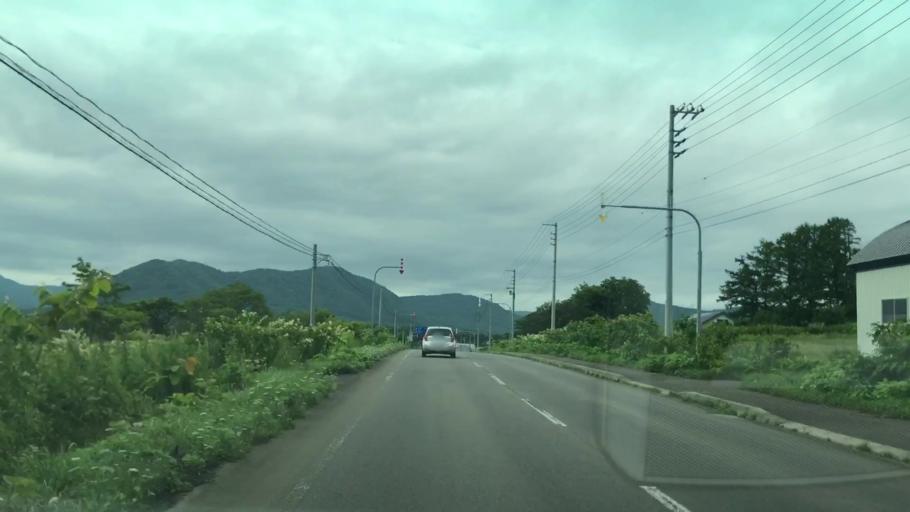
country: JP
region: Hokkaido
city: Yoichi
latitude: 43.0952
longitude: 140.8205
